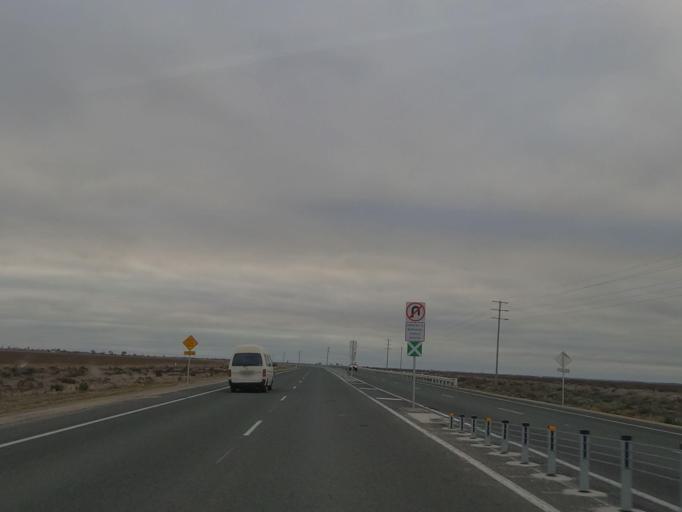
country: AU
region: Victoria
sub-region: Swan Hill
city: Swan Hill
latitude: -35.5115
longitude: 143.7249
